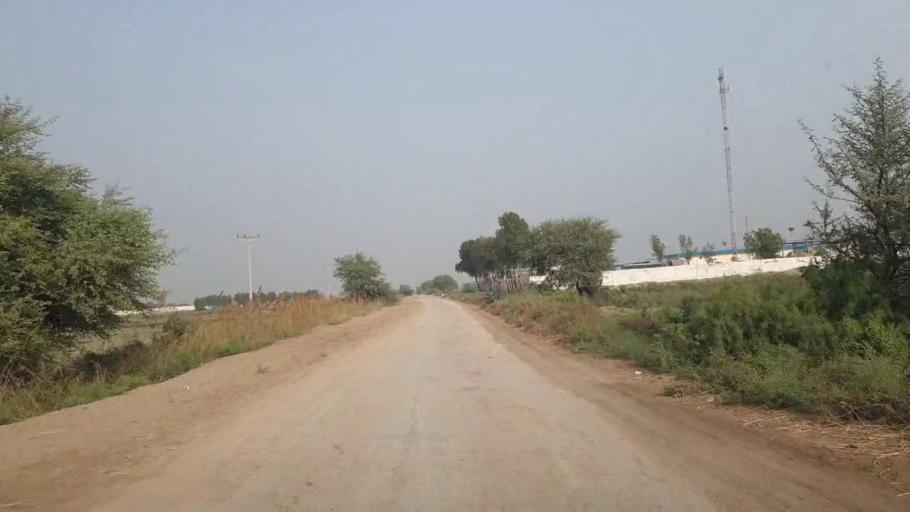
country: PK
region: Sindh
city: Mirpur Batoro
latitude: 24.5673
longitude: 68.4106
